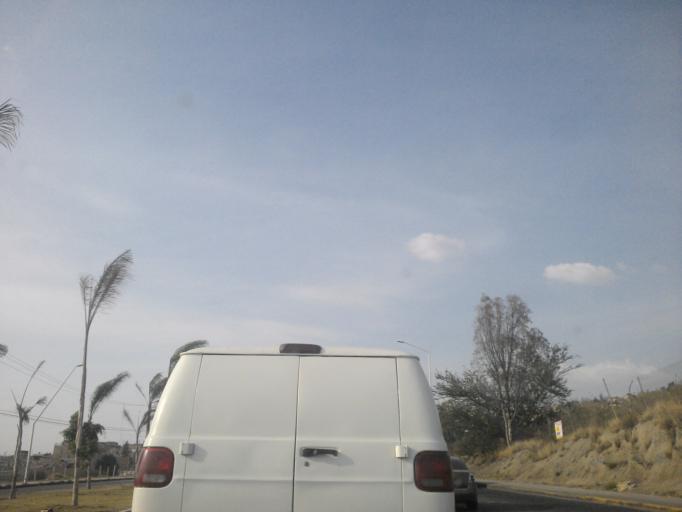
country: MX
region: Jalisco
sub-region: Tlajomulco de Zuniga
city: Altus Bosques
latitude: 20.5954
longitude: -103.3802
